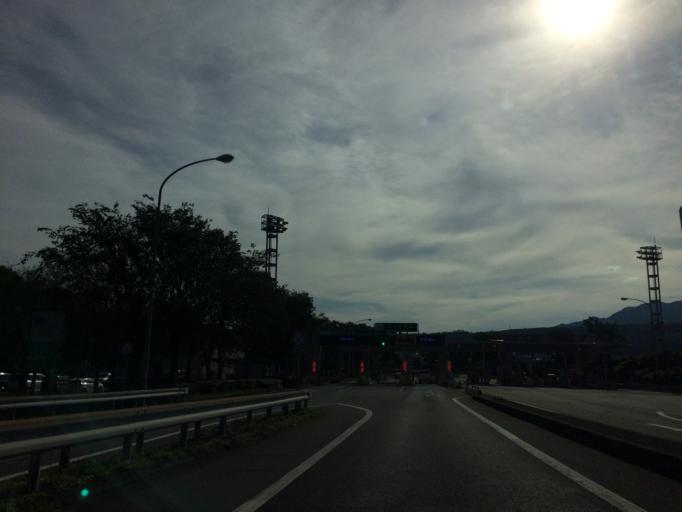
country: JP
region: Gunma
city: Shibukawa
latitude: 36.4779
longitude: 139.0166
